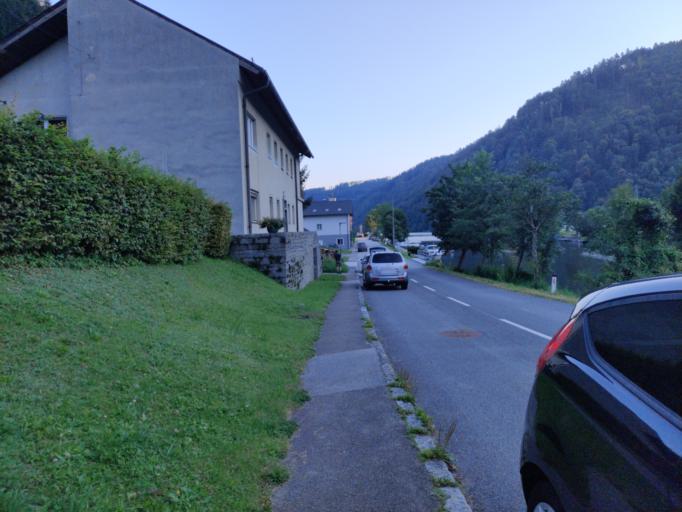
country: AT
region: Upper Austria
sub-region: Politischer Bezirk Rohrbach
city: Atzesberg
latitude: 48.4525
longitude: 13.9214
